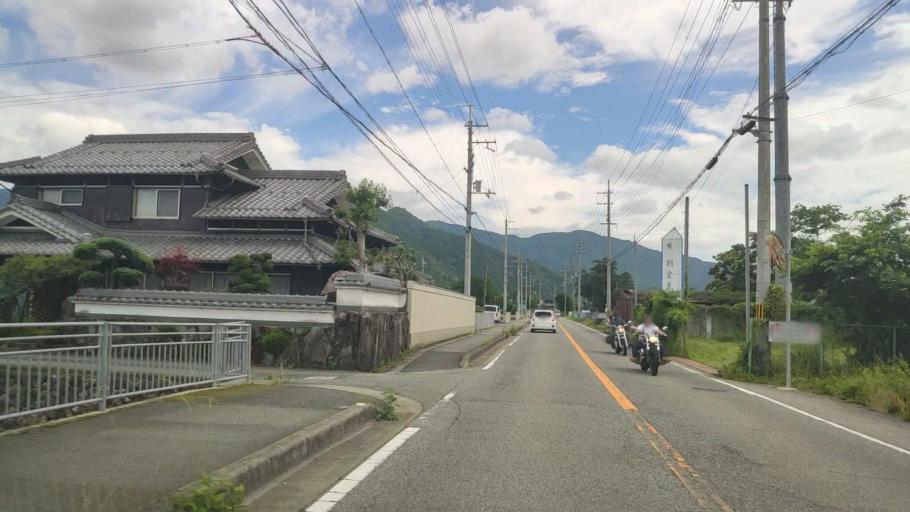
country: JP
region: Hyogo
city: Nishiwaki
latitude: 35.0882
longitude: 134.8924
